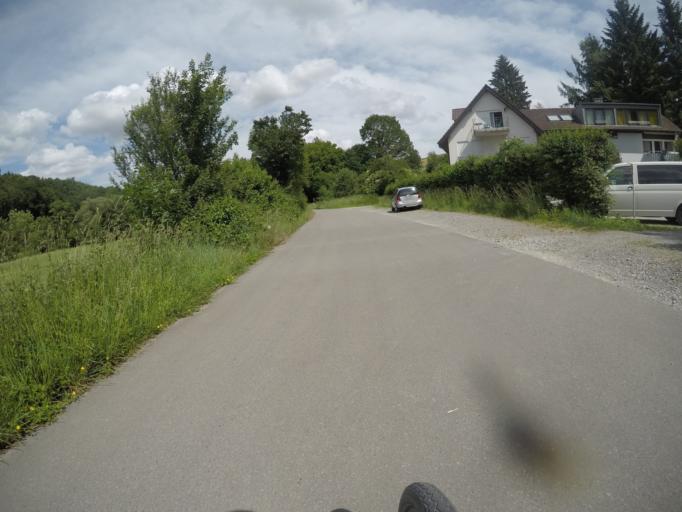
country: DE
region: Baden-Wuerttemberg
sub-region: Regierungsbezirk Stuttgart
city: Waldenbuch
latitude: 48.6342
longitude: 9.1530
